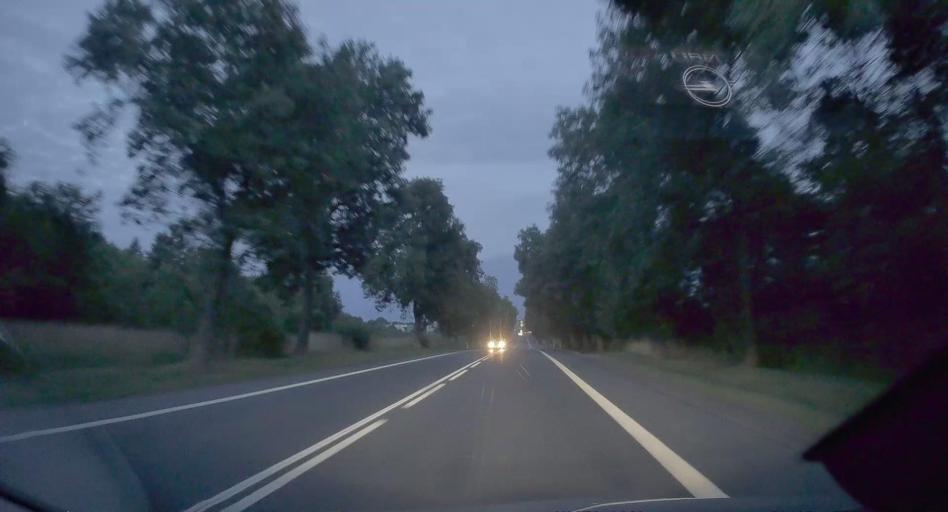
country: PL
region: Silesian Voivodeship
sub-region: Powiat klobucki
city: Klobuck
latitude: 50.9095
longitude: 18.9107
